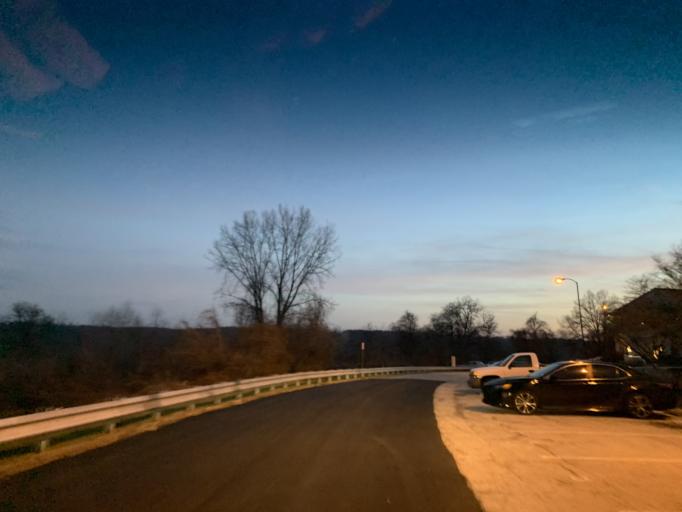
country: US
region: Maryland
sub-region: Baltimore County
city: Carney
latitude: 39.4486
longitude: -76.5158
